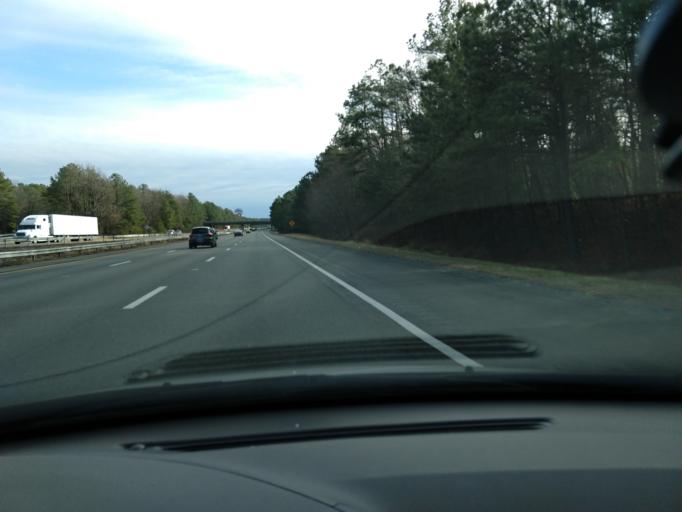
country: US
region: Virginia
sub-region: Hanover County
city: Ashland
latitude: 37.8486
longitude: -77.4542
